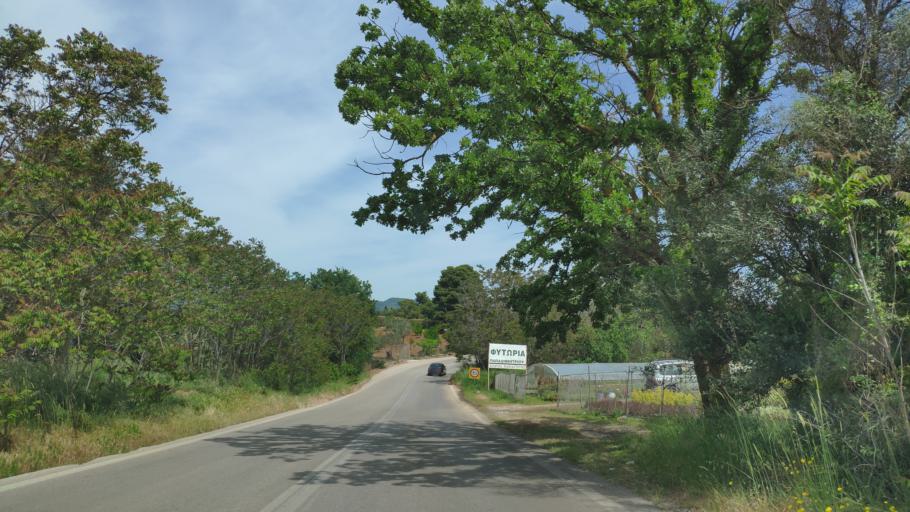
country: GR
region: Attica
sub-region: Nomarchia Anatolikis Attikis
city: Agios Stefanos
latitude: 38.1749
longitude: 23.8603
